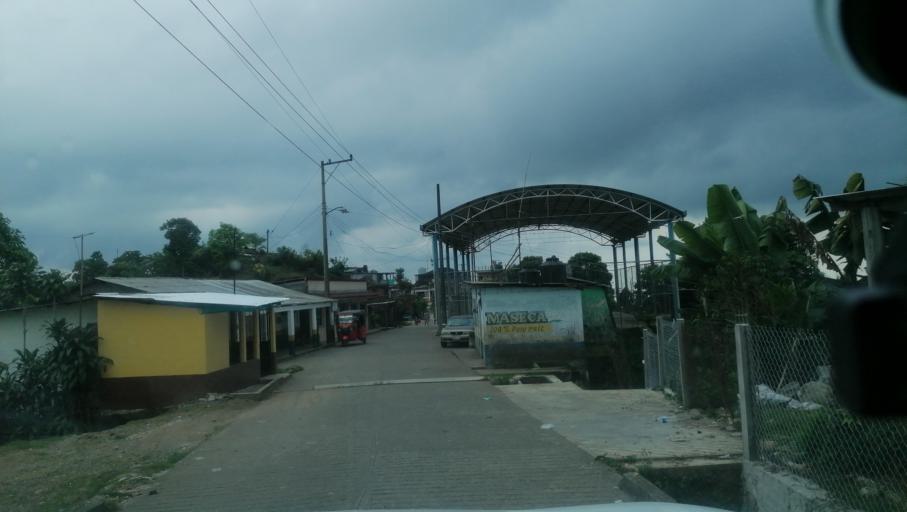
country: MX
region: Chiapas
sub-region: Cacahoatan
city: Benito Juarez
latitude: 15.0847
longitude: -92.1617
